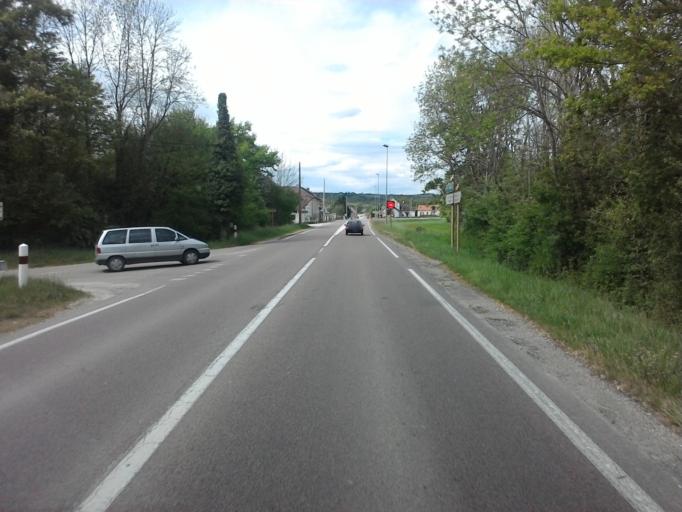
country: FR
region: Bourgogne
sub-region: Departement de l'Yonne
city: Champs-sur-Yonne
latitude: 47.7293
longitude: 3.6008
